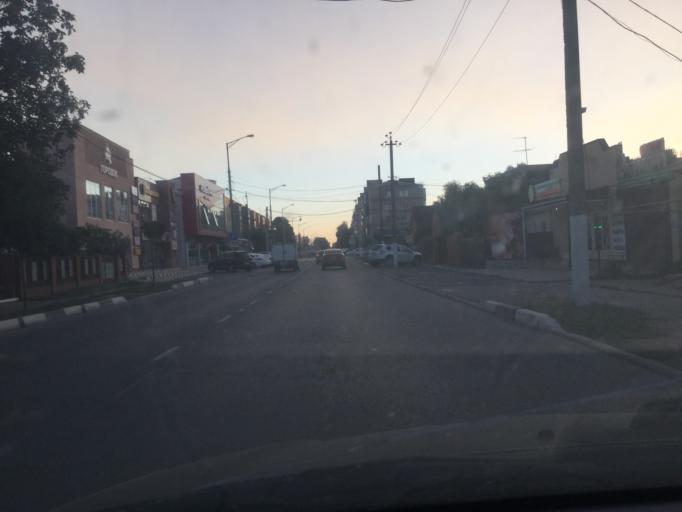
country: RU
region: Krasnodarskiy
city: Slavyansk-na-Kubani
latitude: 45.2558
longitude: 38.1222
